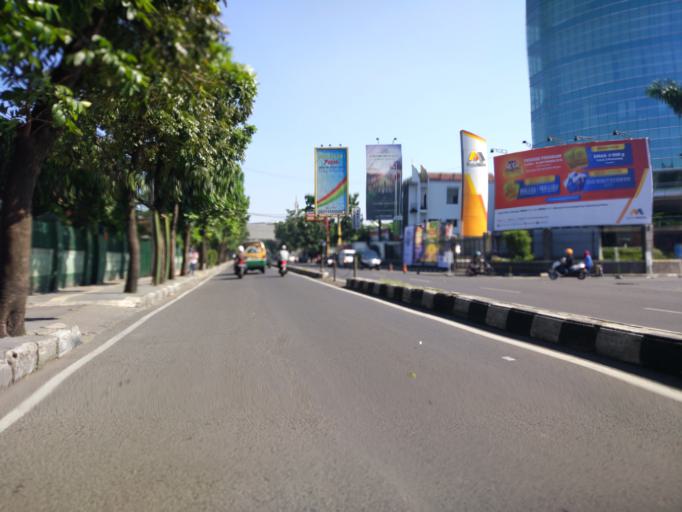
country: ID
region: West Java
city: Bandung
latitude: -6.9274
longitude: 107.6355
